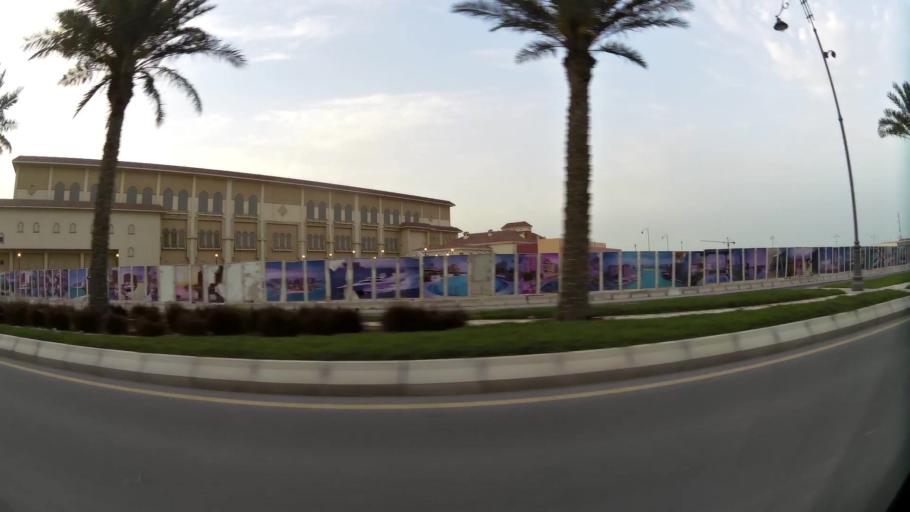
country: QA
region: Baladiyat ad Dawhah
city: Doha
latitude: 25.3711
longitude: 51.5540
